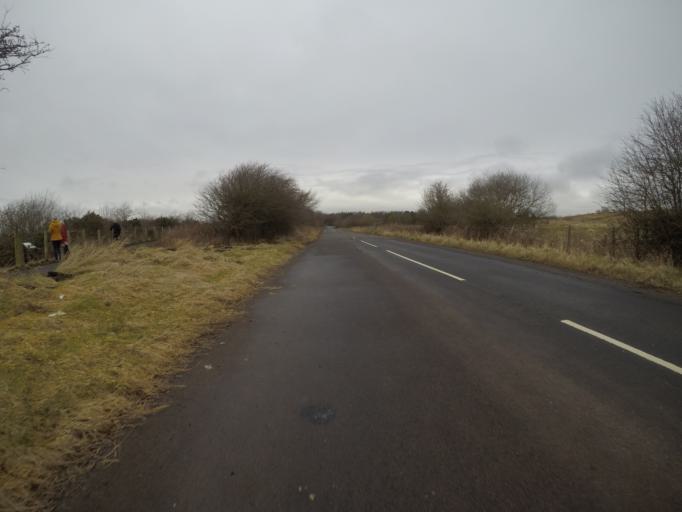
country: GB
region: Scotland
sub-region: North Ayrshire
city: Kilwinning
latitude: 55.6374
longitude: -4.6908
